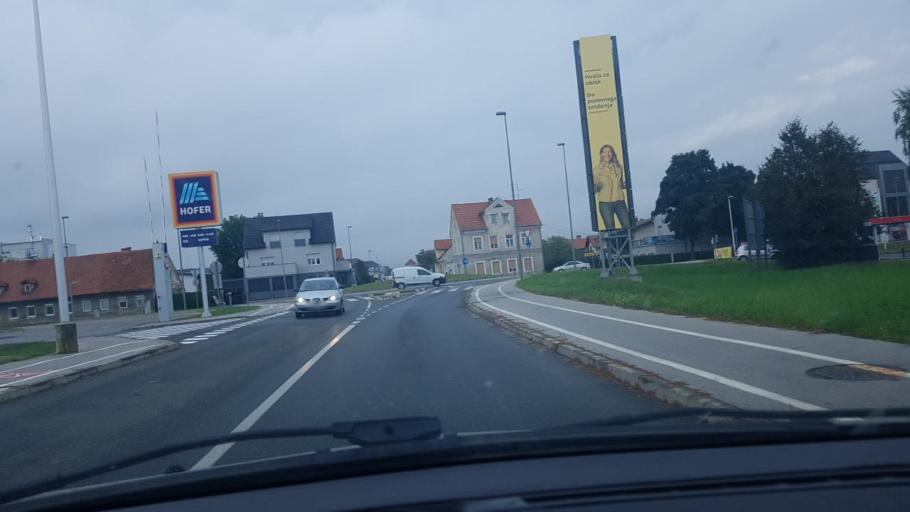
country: SI
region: Ptuj
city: Ptuj
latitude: 46.4165
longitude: 15.8793
